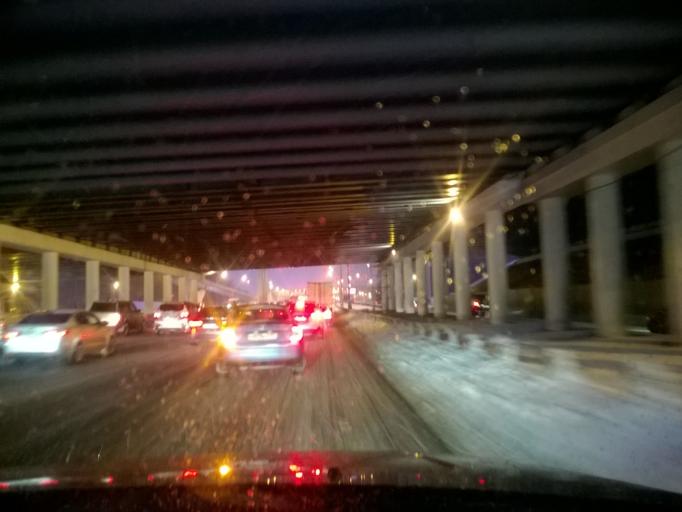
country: RU
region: Moskovskaya
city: Mosrentgen
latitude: 55.6387
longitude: 37.4593
